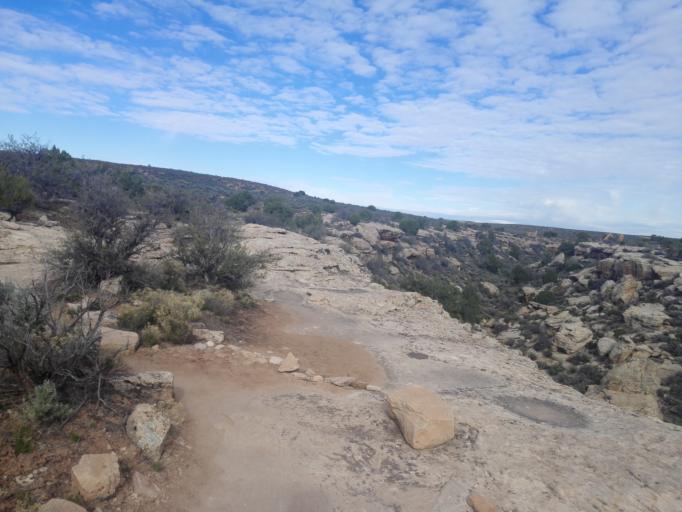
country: US
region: Colorado
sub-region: Montezuma County
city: Towaoc
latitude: 37.3833
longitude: -109.0777
